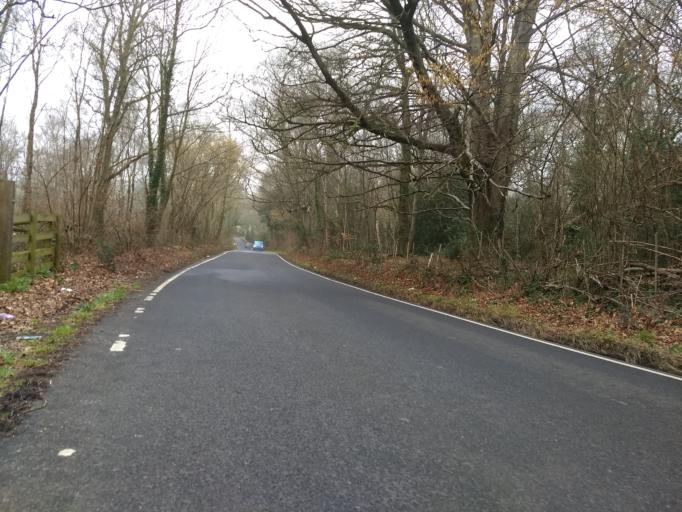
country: GB
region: England
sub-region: Isle of Wight
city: Newport
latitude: 50.7050
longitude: -1.2490
